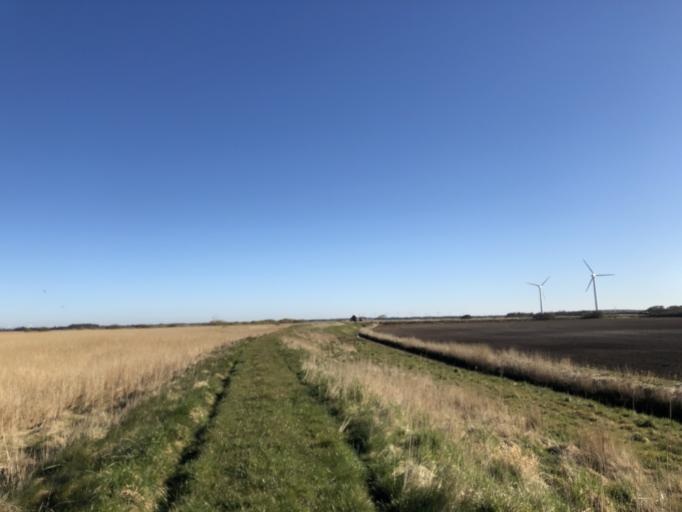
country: DK
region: Central Jutland
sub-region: Holstebro Kommune
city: Ulfborg
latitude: 56.3076
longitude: 8.2926
